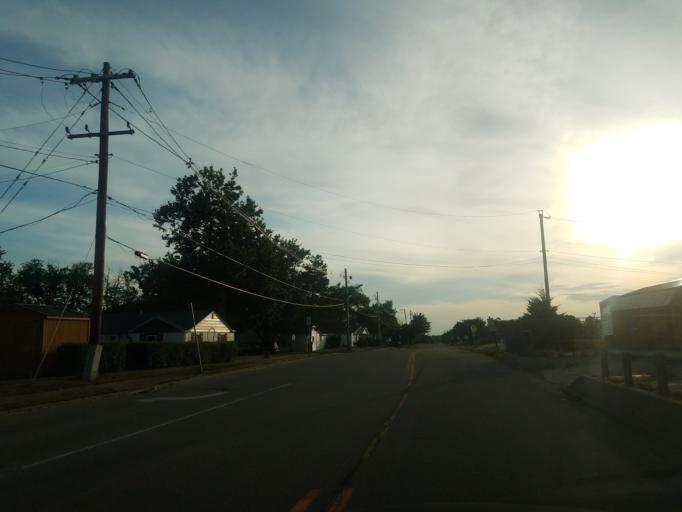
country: US
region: Illinois
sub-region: McLean County
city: Bloomington
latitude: 40.4415
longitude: -88.9914
